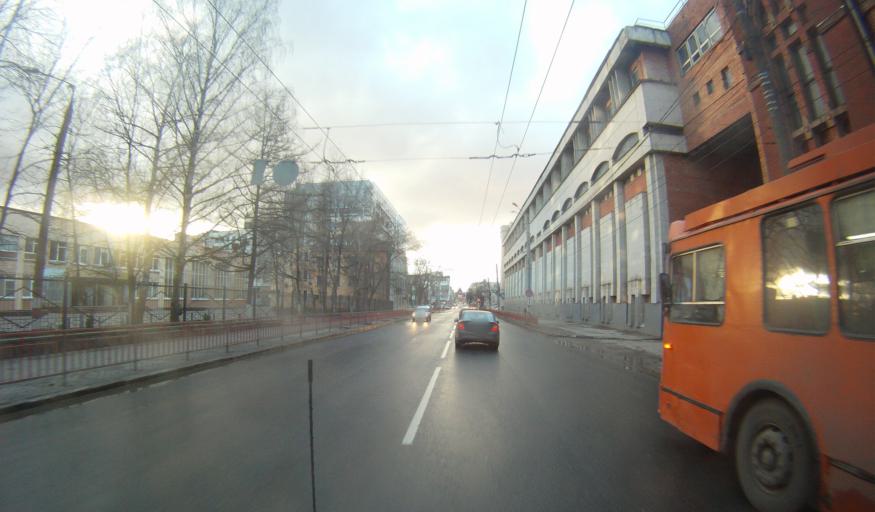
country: RU
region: Nizjnij Novgorod
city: Nizhniy Novgorod
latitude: 56.3211
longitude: 44.0126
